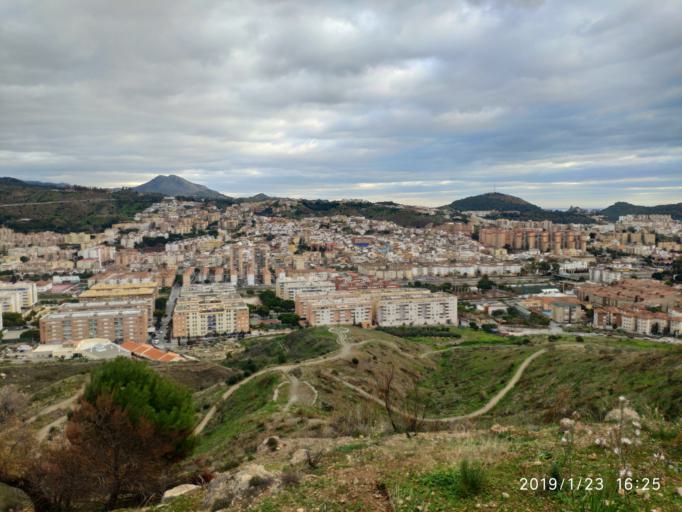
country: ES
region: Andalusia
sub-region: Provincia de Malaga
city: Malaga
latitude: 36.7455
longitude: -4.4320
